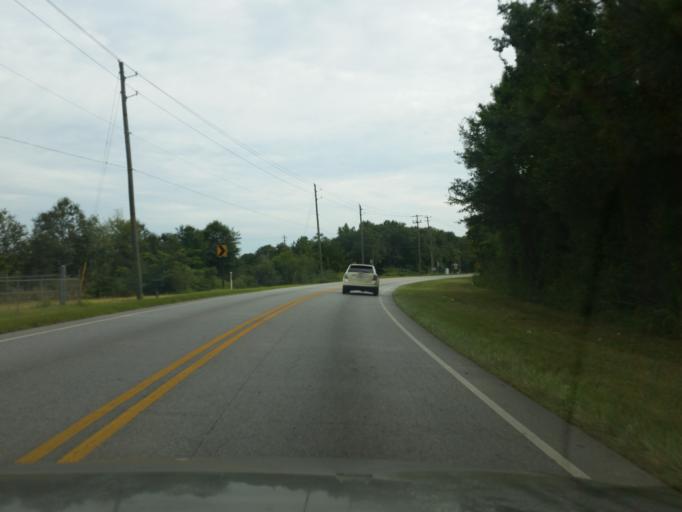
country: US
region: Florida
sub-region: Escambia County
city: Cantonment
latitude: 30.6452
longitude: -87.3173
